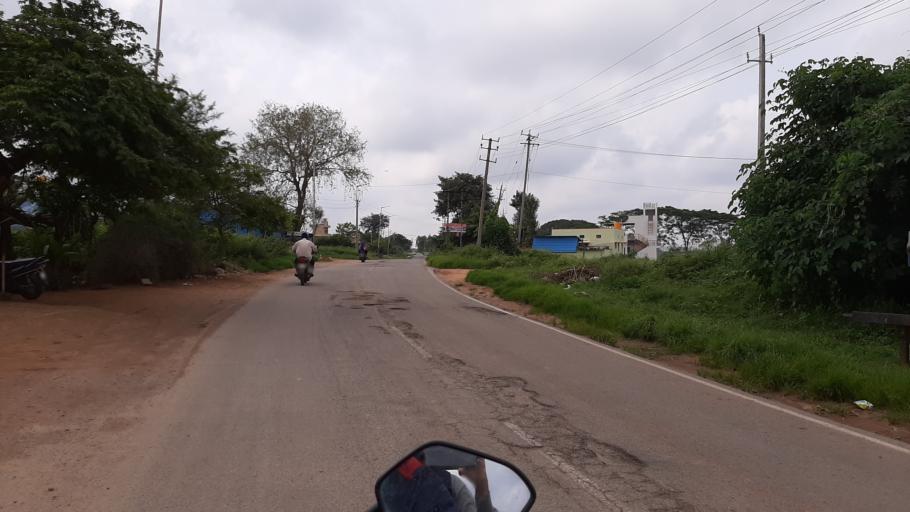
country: IN
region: Karnataka
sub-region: Ramanagara
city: Magadi
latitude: 12.9489
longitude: 77.2381
